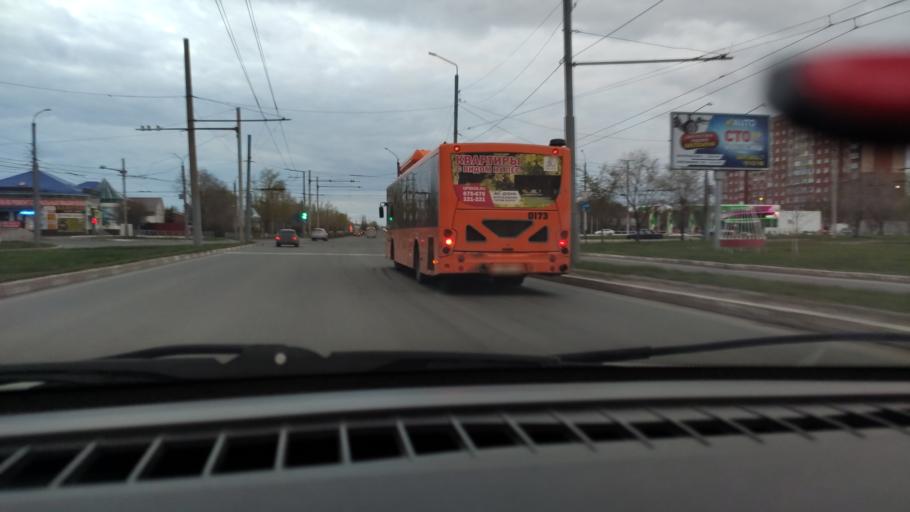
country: RU
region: Orenburg
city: Orenburg
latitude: 51.8179
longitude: 55.1077
